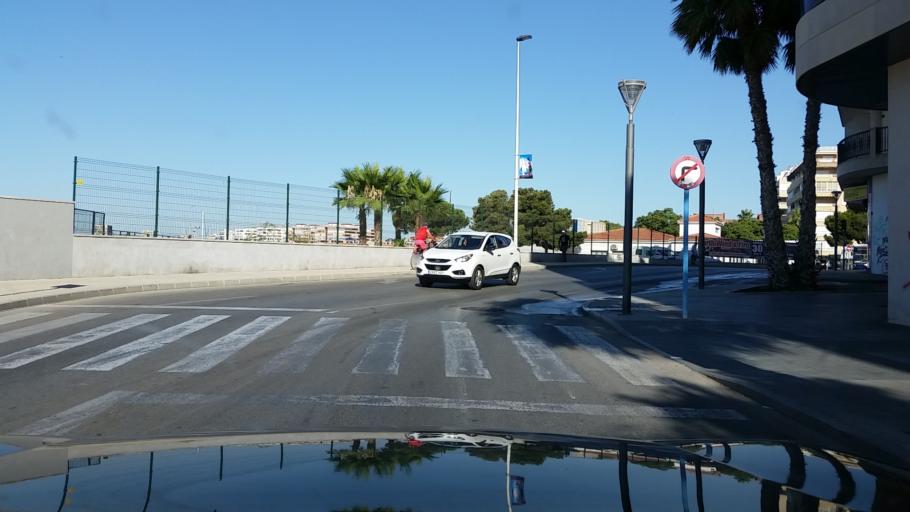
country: ES
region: Valencia
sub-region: Provincia de Alicante
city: Torrevieja
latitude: 37.9756
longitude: -0.6842
